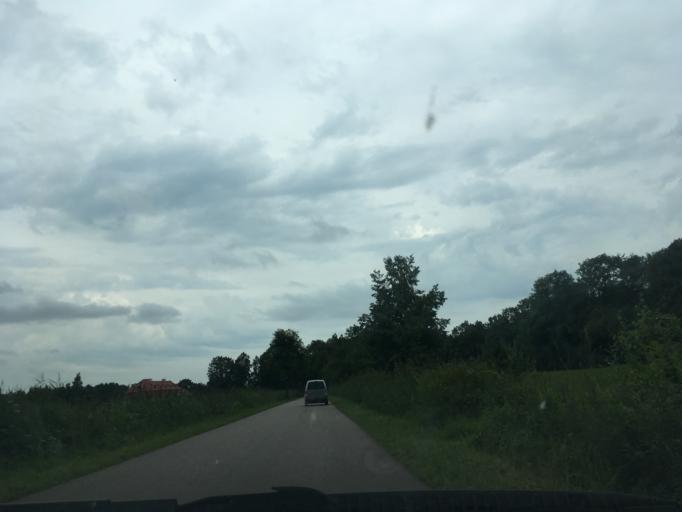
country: PL
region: Warmian-Masurian Voivodeship
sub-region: Powiat wegorzewski
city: Wegorzewo
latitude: 54.1455
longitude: 21.7257
